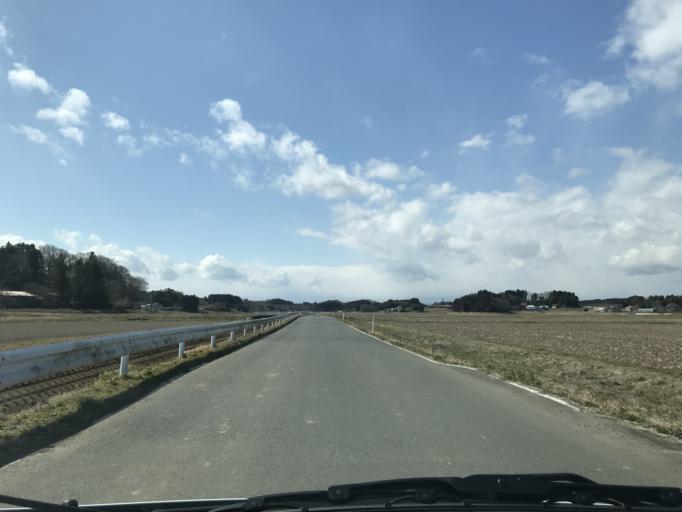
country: JP
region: Miyagi
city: Wakuya
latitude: 38.6758
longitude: 141.1355
